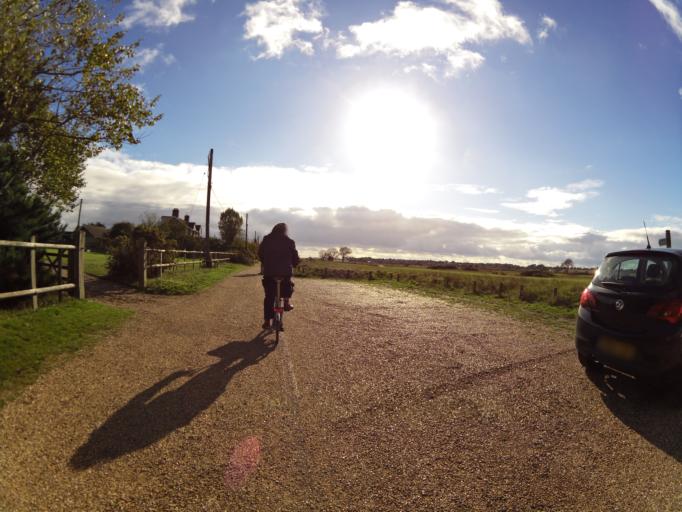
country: GB
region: England
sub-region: Suffolk
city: Felixstowe
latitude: 51.9859
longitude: 1.3889
